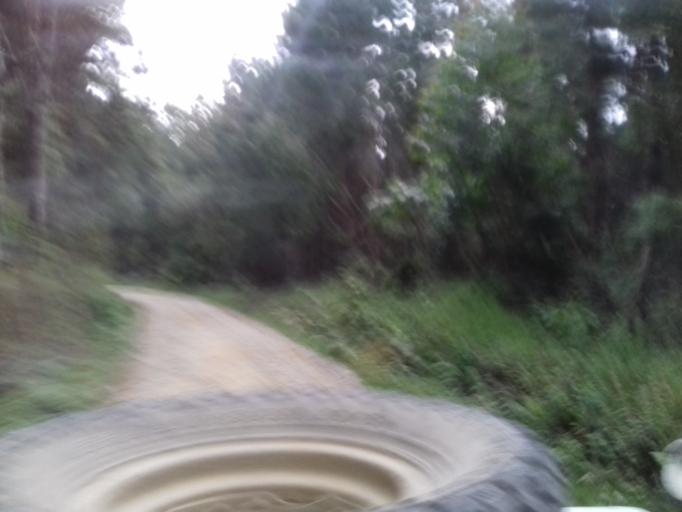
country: CO
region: Quindio
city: Salento
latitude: 4.5982
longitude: -75.5399
